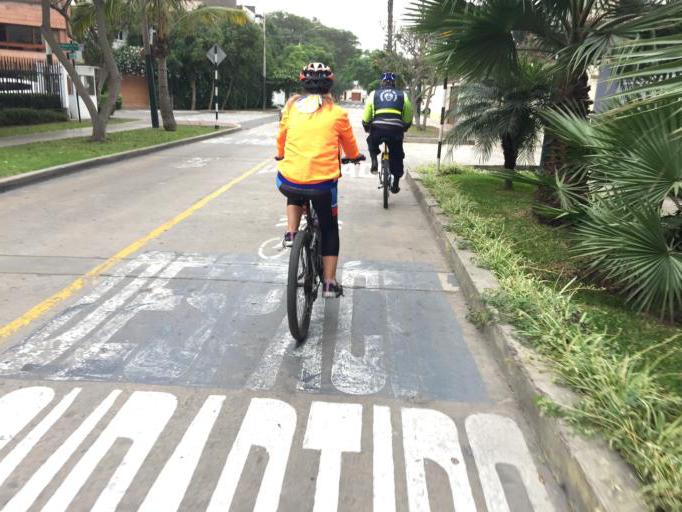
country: PE
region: Lima
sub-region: Lima
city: San Isidro
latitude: -12.0929
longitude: -77.0509
